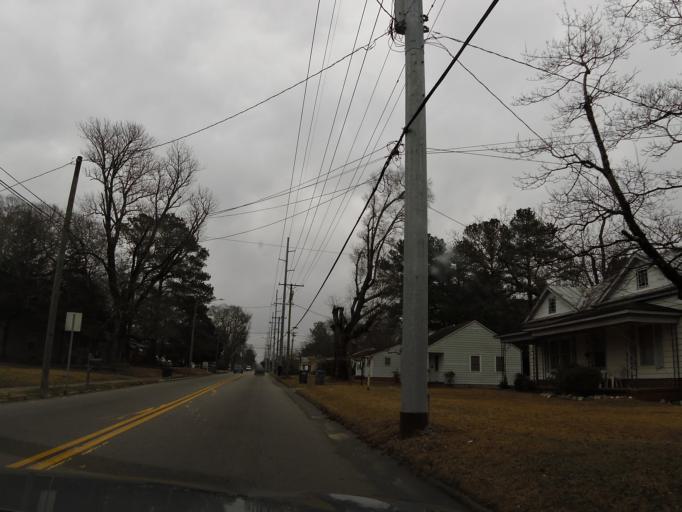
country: US
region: North Carolina
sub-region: Nash County
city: Rocky Mount
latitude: 35.9313
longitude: -77.8214
